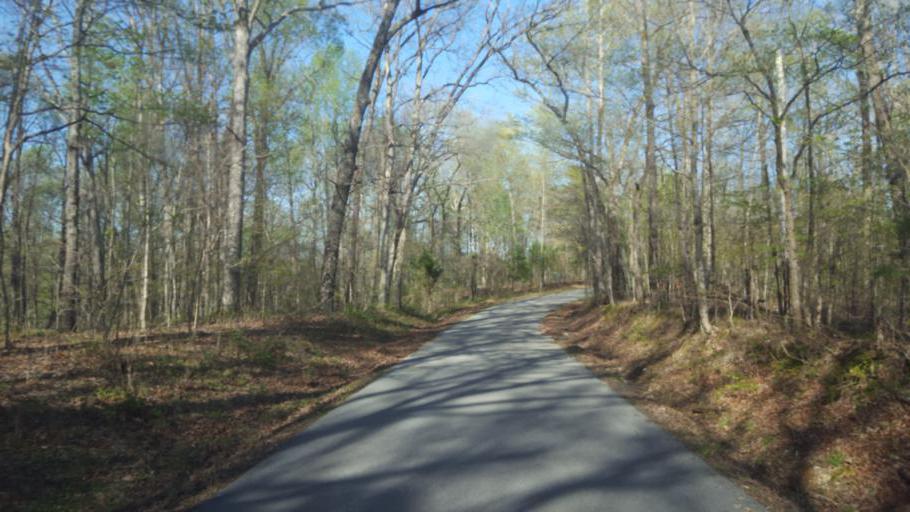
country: US
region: Kentucky
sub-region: Barren County
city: Cave City
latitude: 37.1973
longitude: -86.0435
